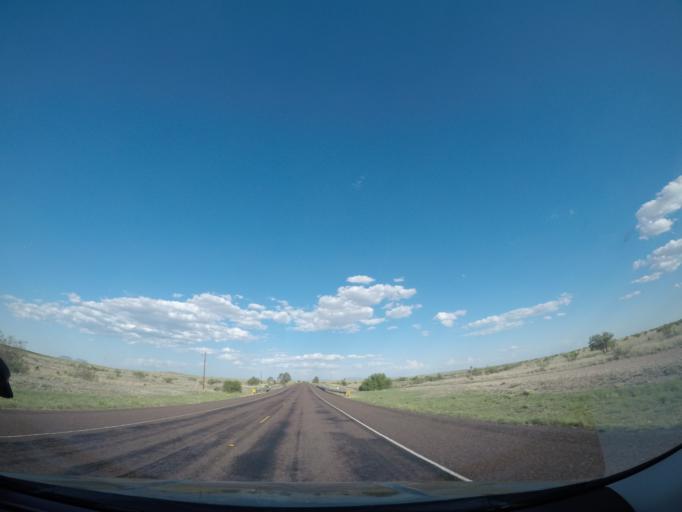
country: US
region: Texas
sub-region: Presidio County
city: Marfa
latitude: 30.3370
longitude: -104.1303
